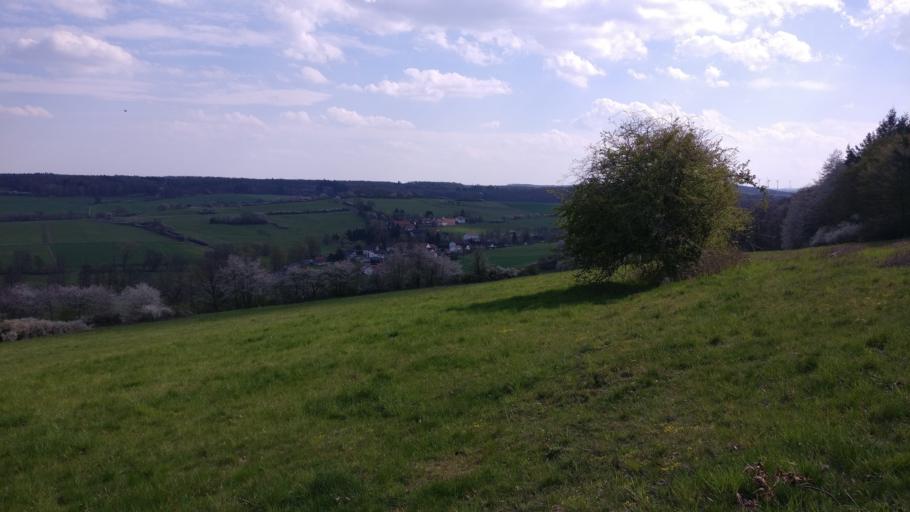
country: DE
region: Hesse
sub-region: Regierungsbezirk Giessen
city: Alsfeld
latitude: 50.6934
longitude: 9.2961
